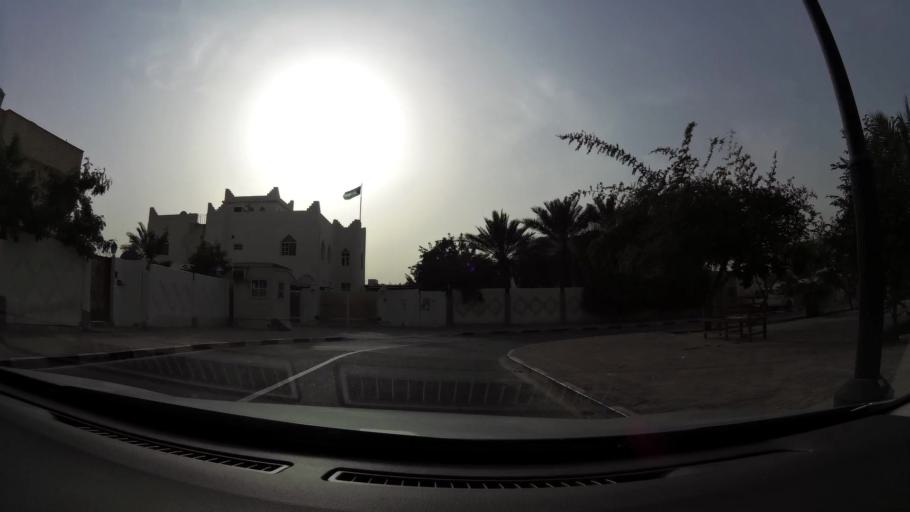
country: QA
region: Baladiyat ad Dawhah
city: Doha
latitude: 25.3275
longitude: 51.5177
